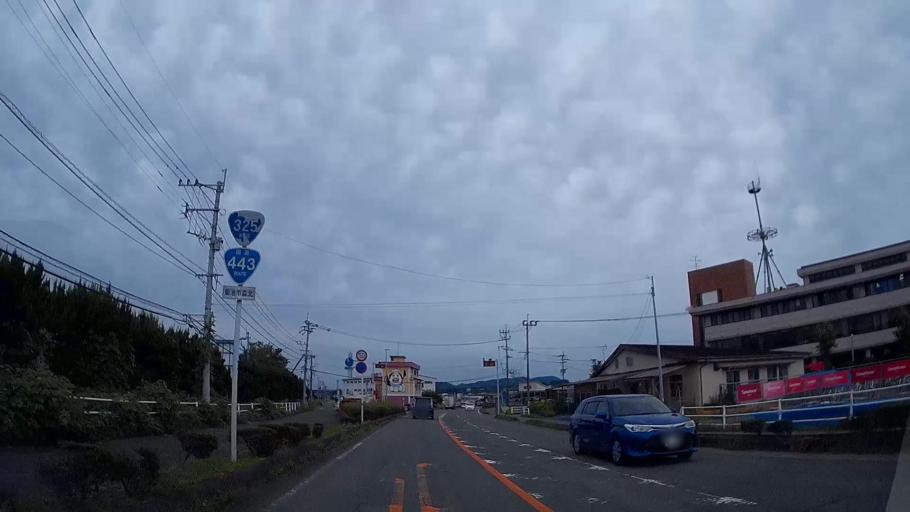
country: JP
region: Kumamoto
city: Kikuchi
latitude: 32.9609
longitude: 130.8169
